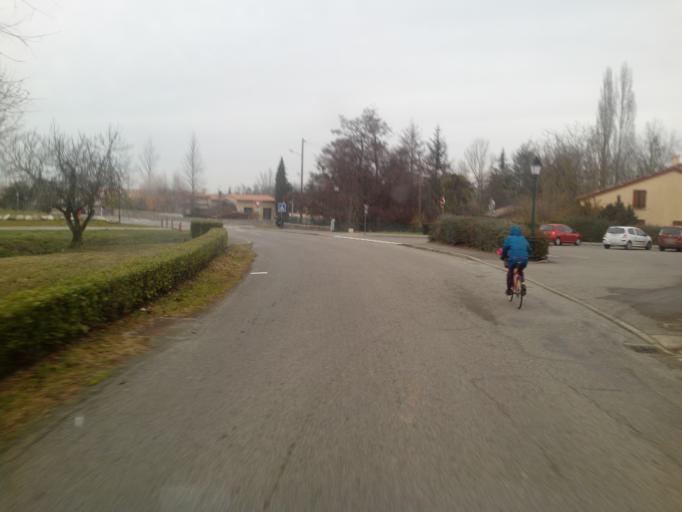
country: FR
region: Midi-Pyrenees
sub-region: Departement de l'Ariege
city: Varilhes
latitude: 43.0587
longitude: 1.6111
